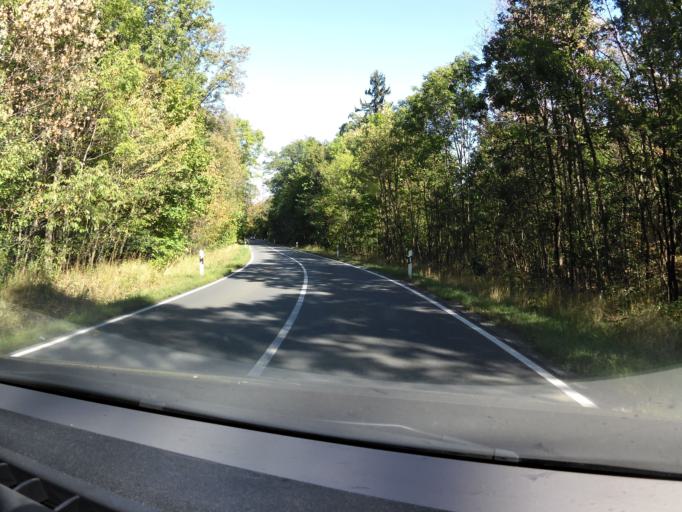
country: DE
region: Saxony-Anhalt
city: Gernrode
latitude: 51.7173
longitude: 11.1411
